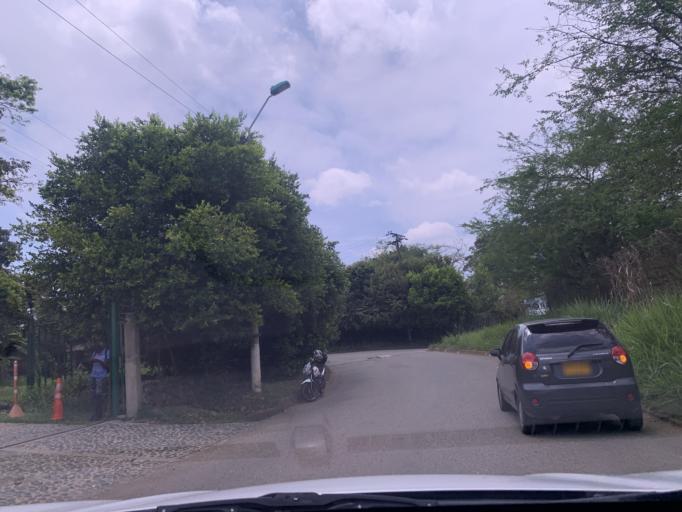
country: CO
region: Valle del Cauca
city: Jamundi
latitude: 3.3361
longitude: -76.5511
